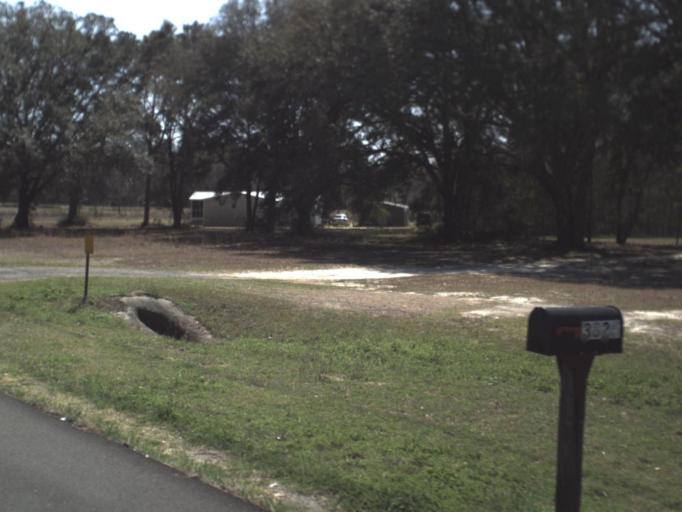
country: US
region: Florida
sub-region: Jackson County
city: Malone
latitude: 30.8430
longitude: -85.0667
